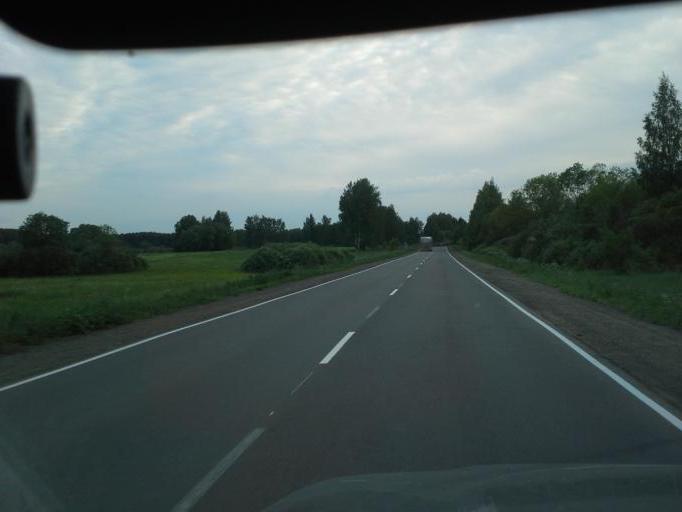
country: RU
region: Ivanovo
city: Petrovskiy
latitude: 56.6222
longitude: 40.2715
